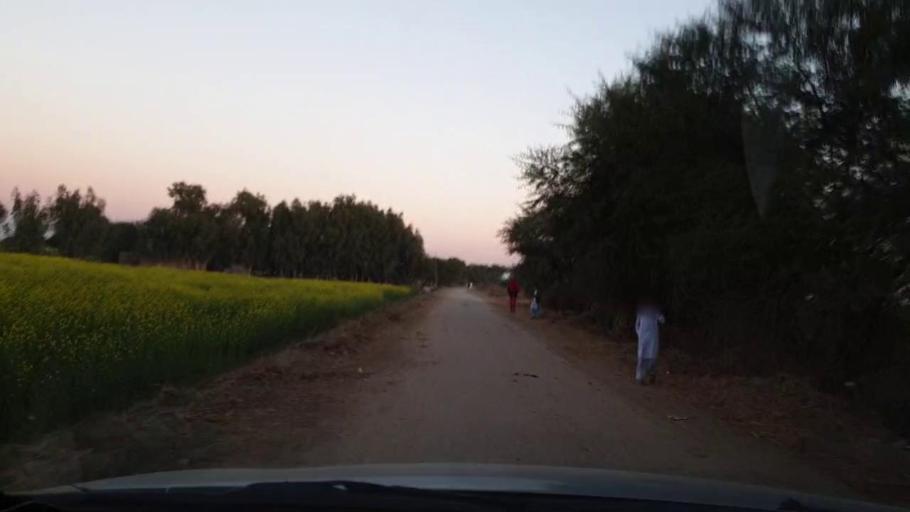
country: PK
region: Sindh
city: Jhol
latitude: 25.9170
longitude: 68.8964
